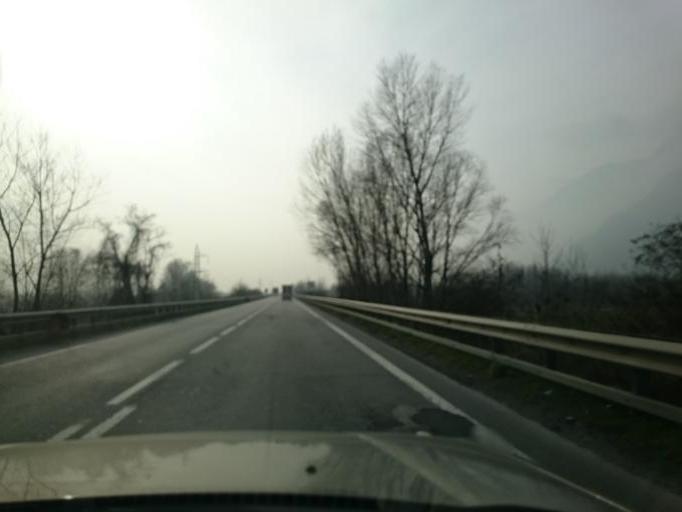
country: IT
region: Lombardy
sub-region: Provincia di Brescia
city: Artogne
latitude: 45.8592
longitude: 10.1524
